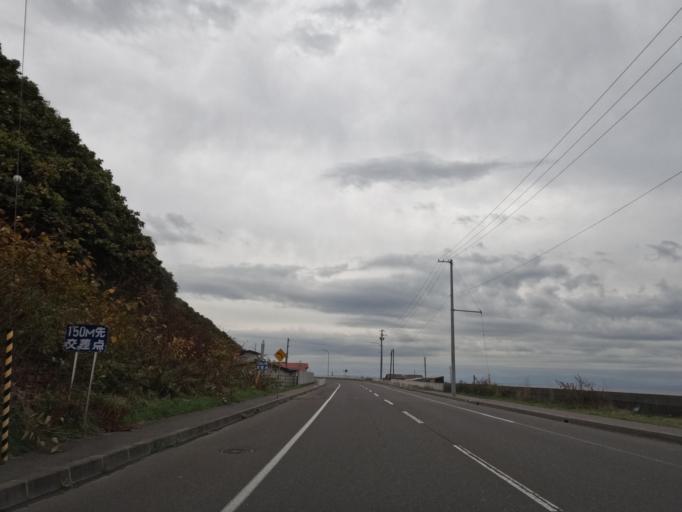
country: JP
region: Hokkaido
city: Date
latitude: 42.3783
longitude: 140.9089
